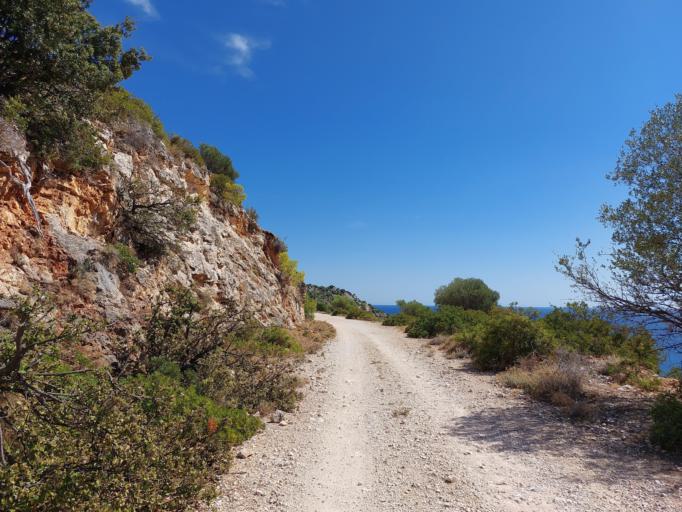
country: HR
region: Dubrovacko-Neretvanska
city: Smokvica
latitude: 42.7342
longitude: 16.8363
